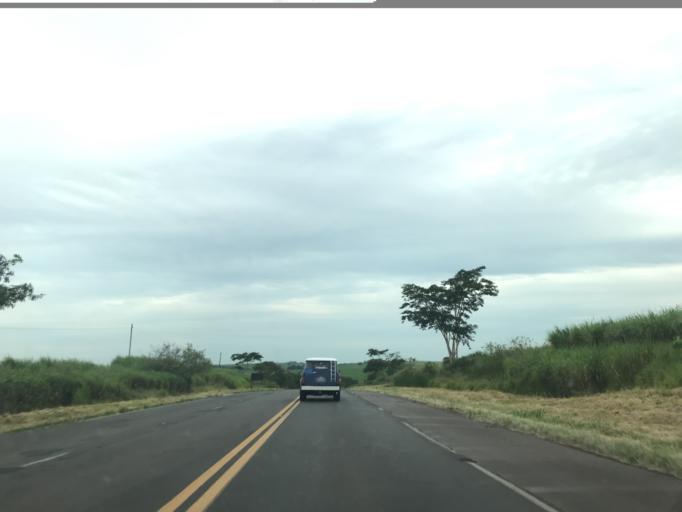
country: BR
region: Sao Paulo
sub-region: Tupa
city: Tupa
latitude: -21.6243
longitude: -50.4853
